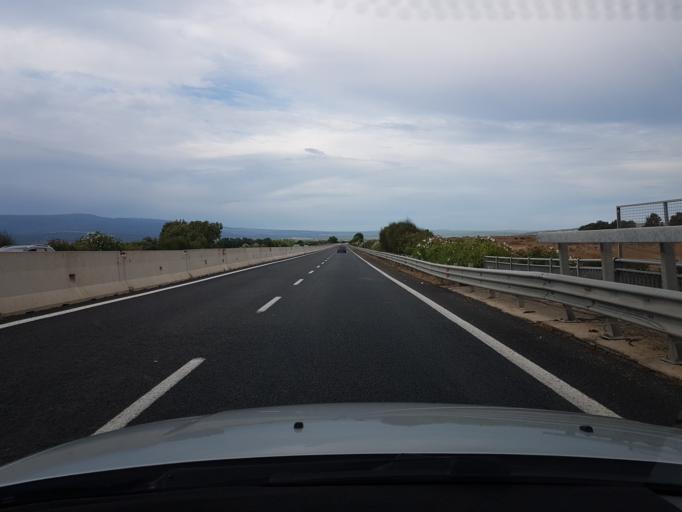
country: IT
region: Sardinia
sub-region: Provincia di Oristano
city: Siamaggiore
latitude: 39.9759
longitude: 8.6286
